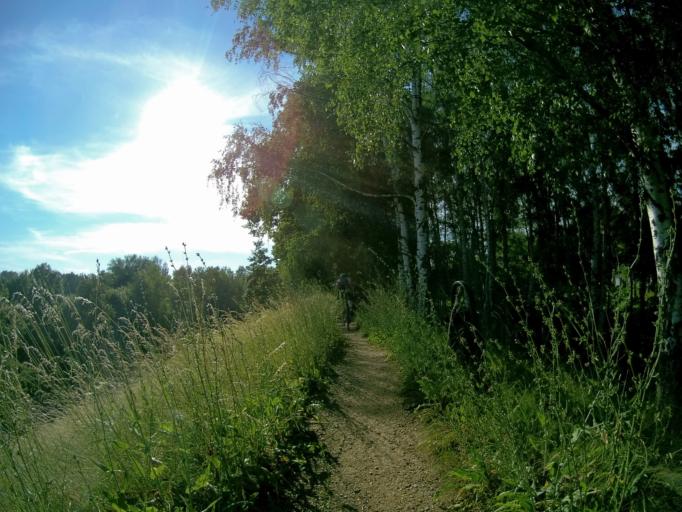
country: RU
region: Ivanovo
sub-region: Privolzhskiy Rayon
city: Ples
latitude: 57.4576
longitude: 41.5145
